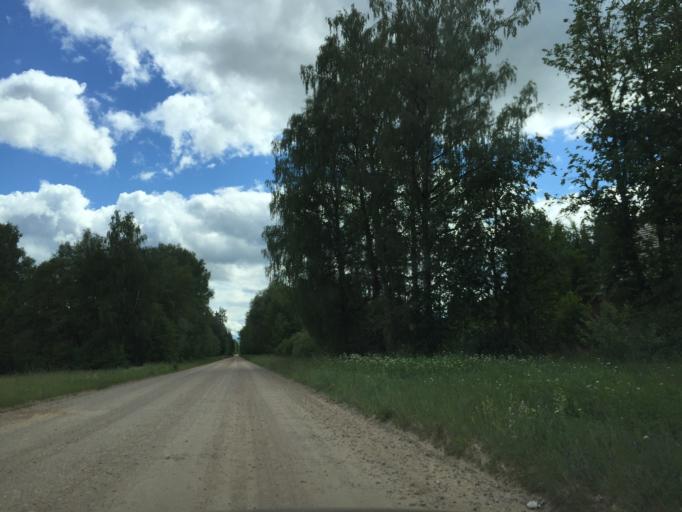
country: LV
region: Lecava
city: Iecava
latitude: 56.5506
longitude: 24.3585
